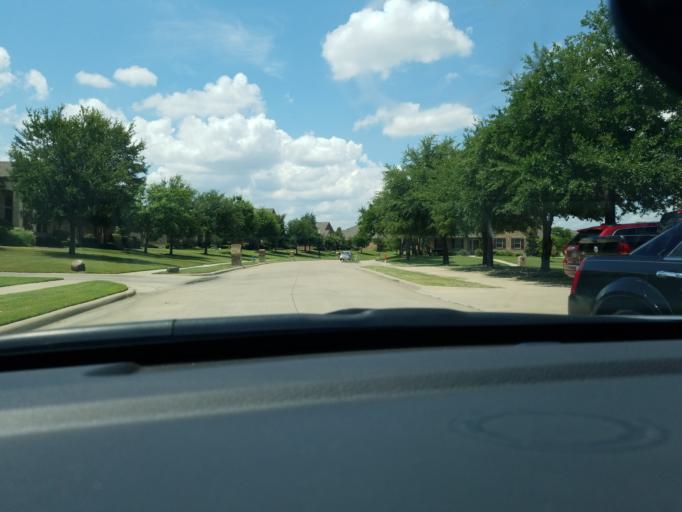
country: US
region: Texas
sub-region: Dallas County
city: Sunnyvale
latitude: 32.8109
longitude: -96.5763
